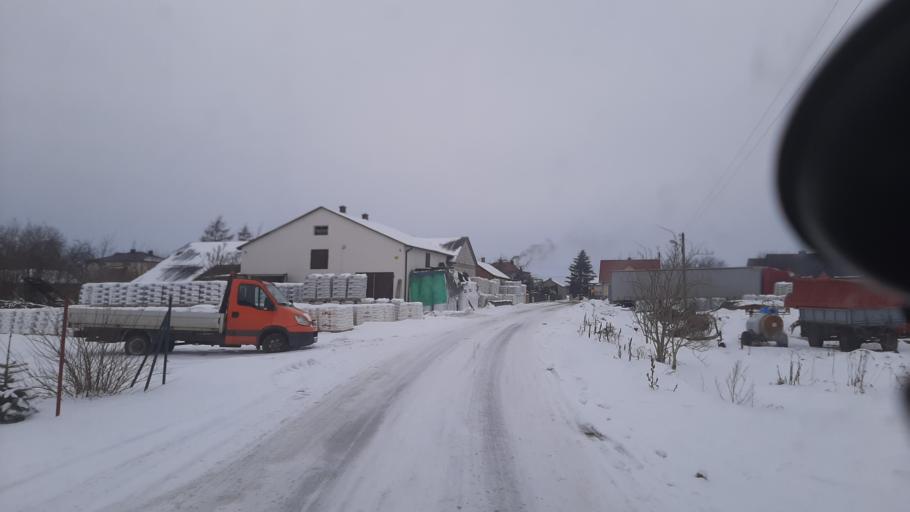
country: PL
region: Lublin Voivodeship
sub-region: Powiat lubelski
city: Garbow
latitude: 51.3585
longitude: 22.3764
